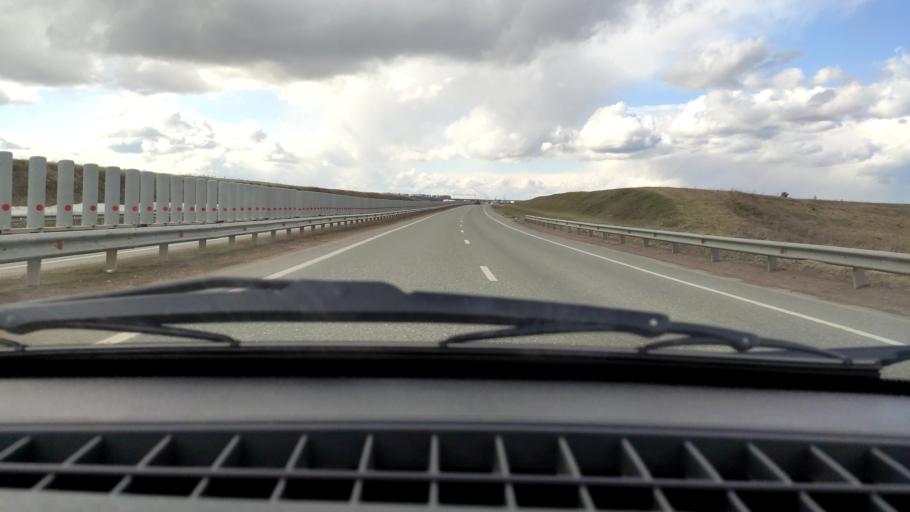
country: RU
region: Bashkortostan
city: Kushnarenkovo
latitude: 55.0668
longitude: 55.3021
